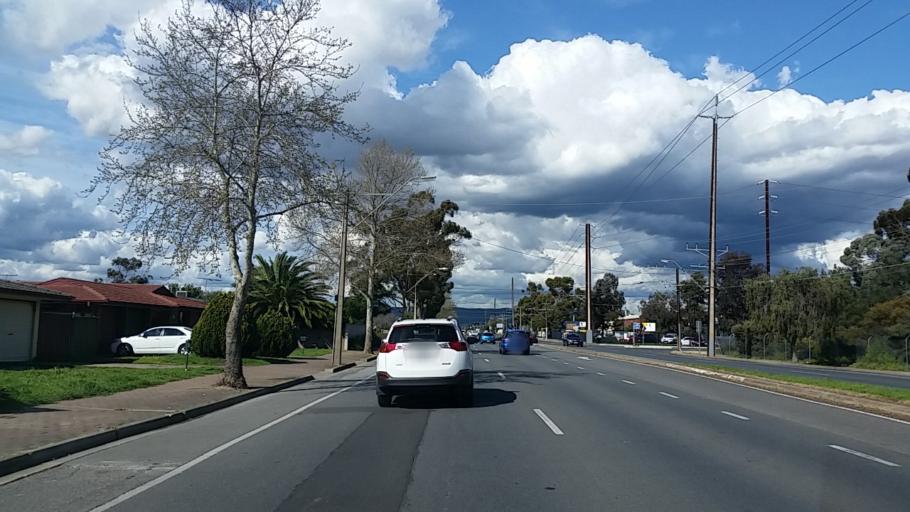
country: AU
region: South Australia
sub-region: Port Adelaide Enfield
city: Gilles Plains
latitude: -34.8459
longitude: 138.6522
